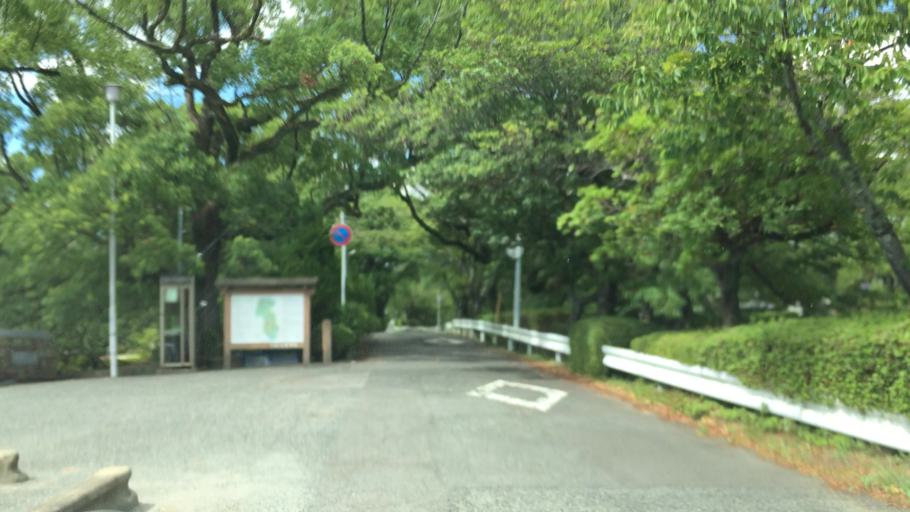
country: JP
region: Saga Prefecture
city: Saga-shi
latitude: 33.2652
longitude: 130.2829
